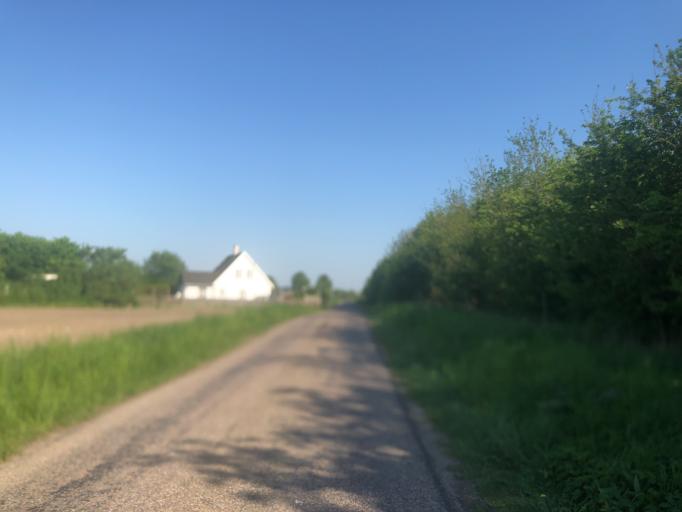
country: DK
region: Zealand
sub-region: Ringsted Kommune
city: Ringsted
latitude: 55.4730
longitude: 11.8207
